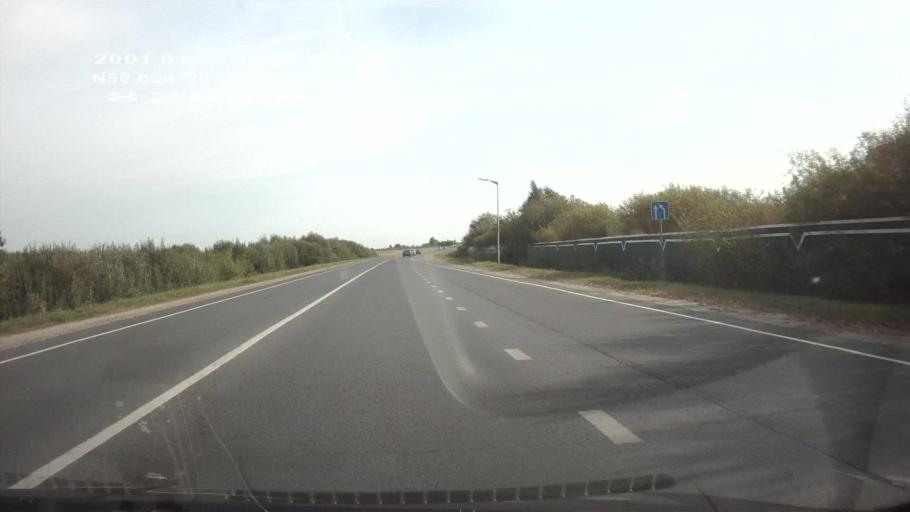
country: RU
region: Mariy-El
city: Yoshkar-Ola
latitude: 56.6541
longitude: 47.9555
